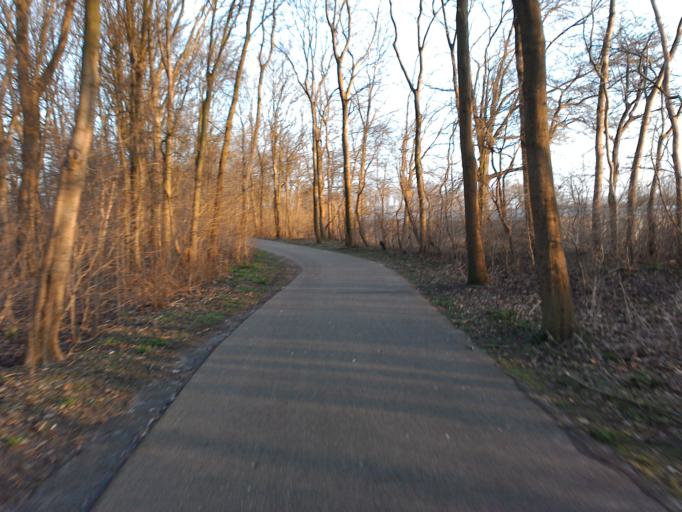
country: NL
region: Utrecht
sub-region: Stichtse Vecht
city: Maarssen
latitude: 52.1369
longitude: 5.0920
